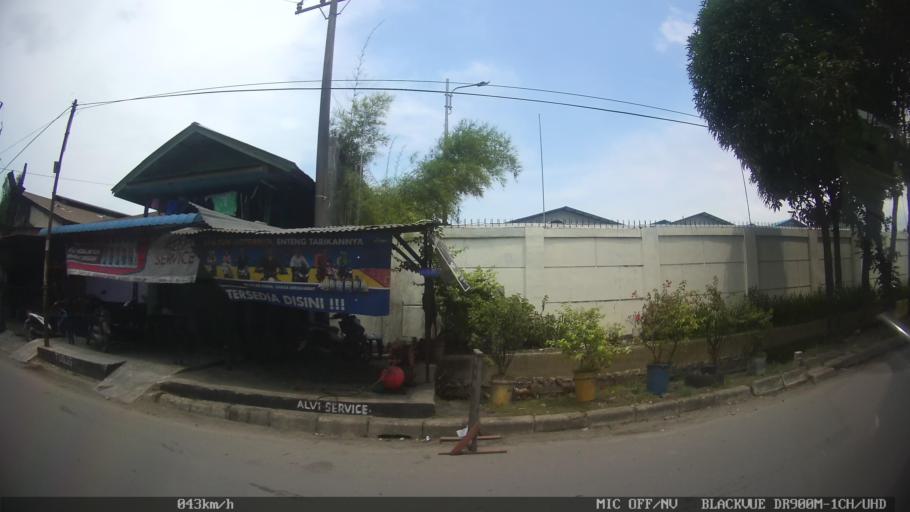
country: ID
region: North Sumatra
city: Labuhan Deli
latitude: 3.6649
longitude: 98.6667
